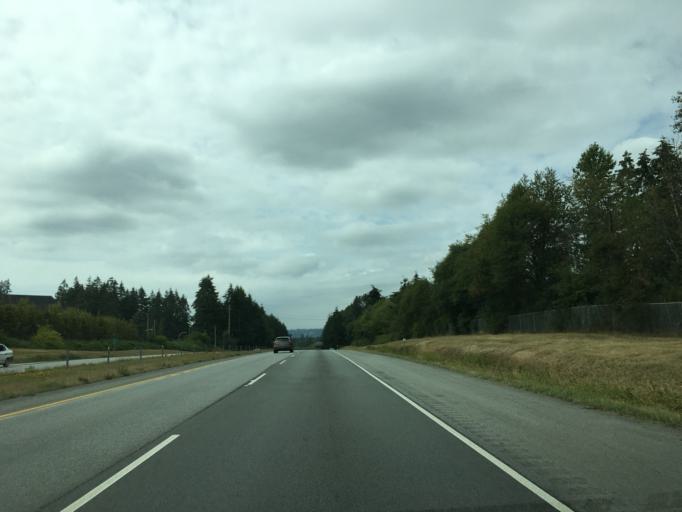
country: CA
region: British Columbia
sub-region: Greater Vancouver Regional District
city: White Rock
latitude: 49.0482
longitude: -122.7881
